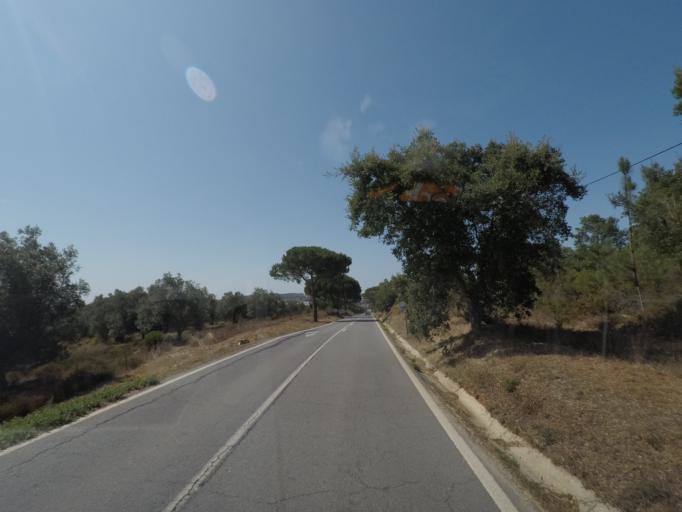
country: PT
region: Beja
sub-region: Odemira
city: Sao Teotonio
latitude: 37.5212
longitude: -8.7021
